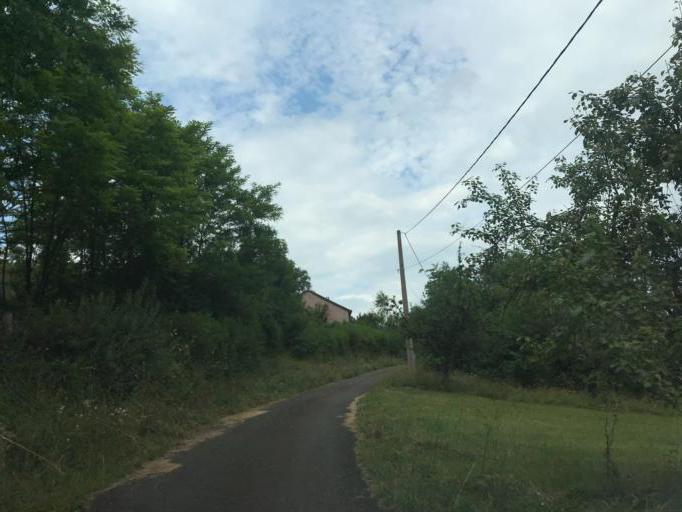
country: FR
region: Franche-Comte
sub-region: Departement du Jura
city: Longchaumois
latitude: 46.4694
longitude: 5.8980
